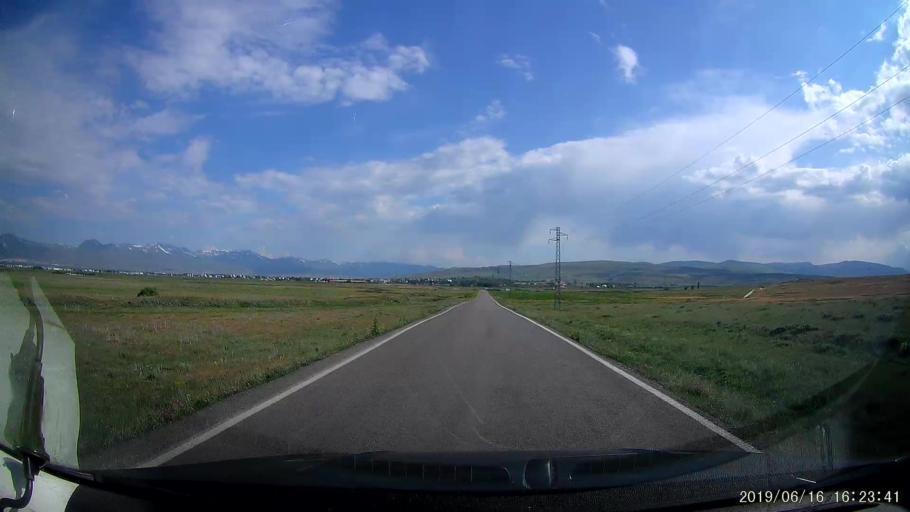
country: TR
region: Erzurum
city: Ilica
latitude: 39.9751
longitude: 41.1056
